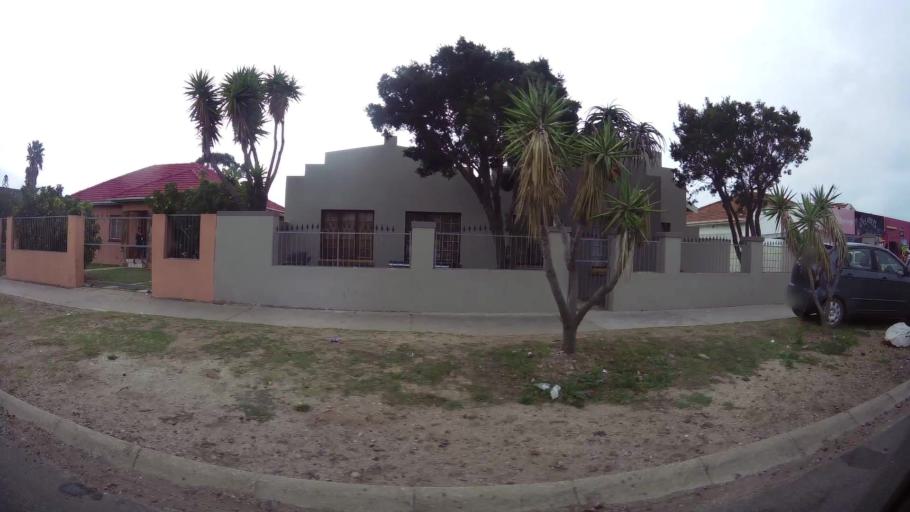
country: ZA
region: Eastern Cape
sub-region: Nelson Mandela Bay Metropolitan Municipality
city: Port Elizabeth
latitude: -33.9008
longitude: 25.5601
